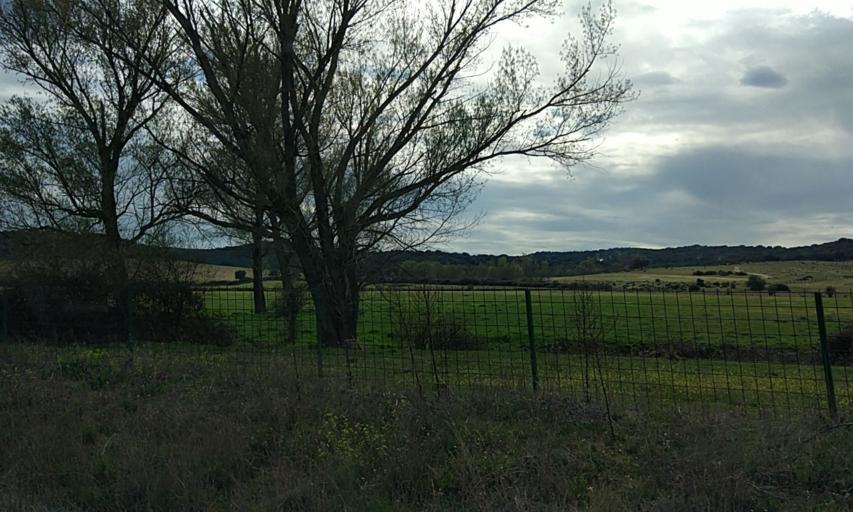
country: ES
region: Castille and Leon
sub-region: Provincia de Salamanca
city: Pastores
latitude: 40.5184
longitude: -6.5674
